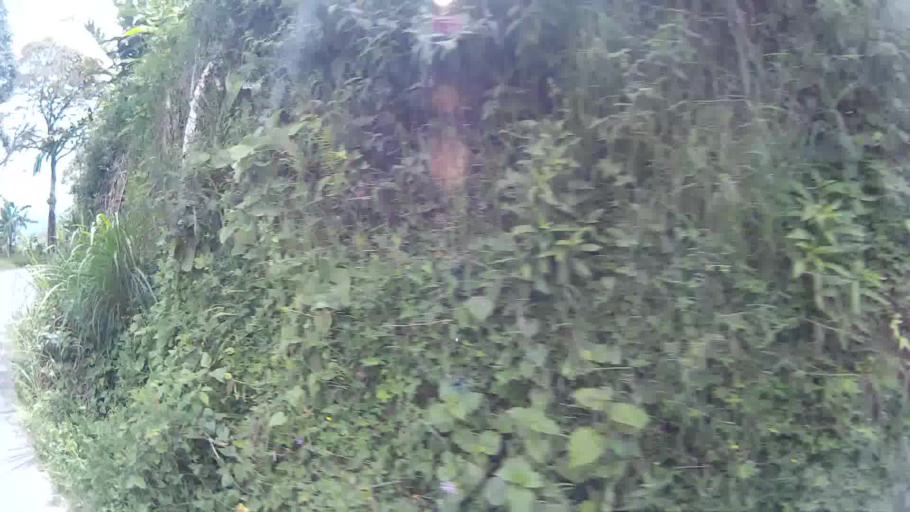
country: CO
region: Risaralda
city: Marsella
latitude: 4.8951
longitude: -75.7467
